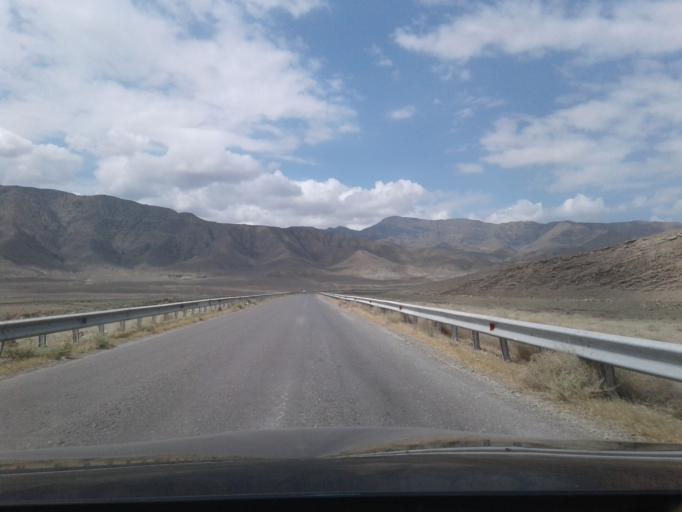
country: TM
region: Ahal
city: Baharly
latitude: 38.5060
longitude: 57.1257
